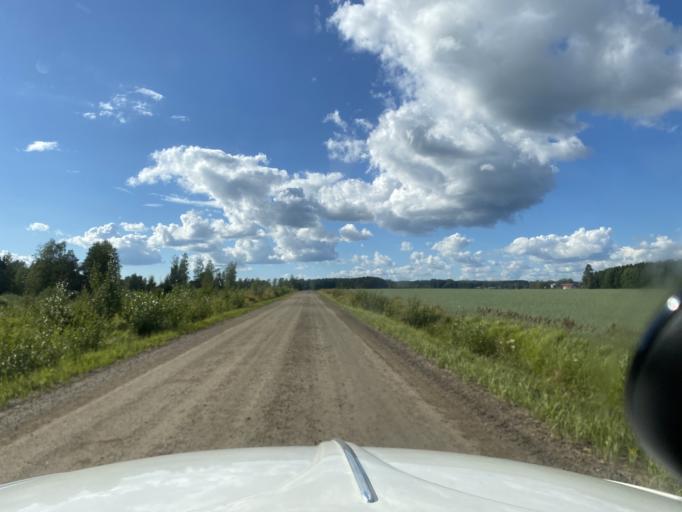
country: FI
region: Pirkanmaa
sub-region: Lounais-Pirkanmaa
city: Punkalaidun
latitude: 61.1324
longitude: 23.2346
